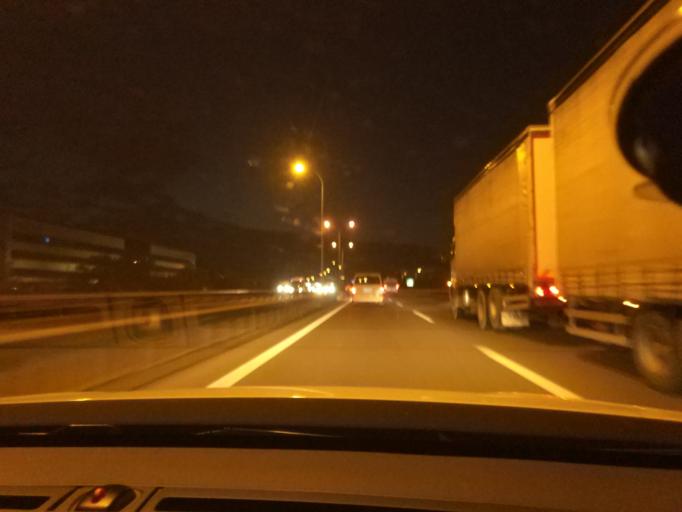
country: TR
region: Istanbul
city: Samandira
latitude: 40.9767
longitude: 29.2278
